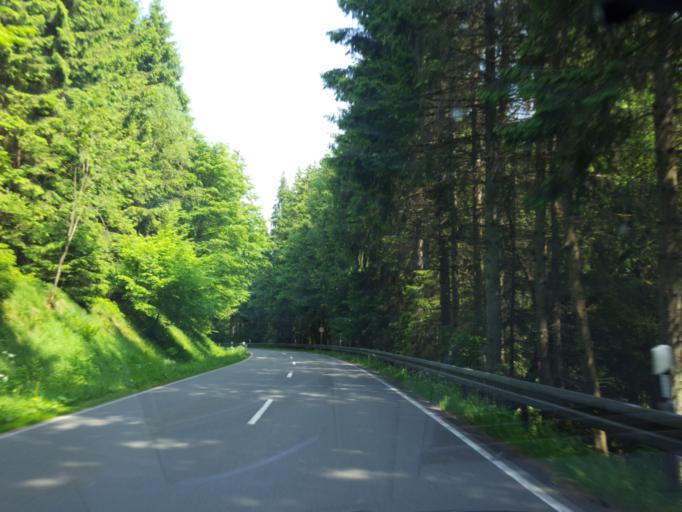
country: DE
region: North Rhine-Westphalia
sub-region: Regierungsbezirk Arnsberg
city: Olsberg
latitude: 51.3149
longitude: 8.4492
